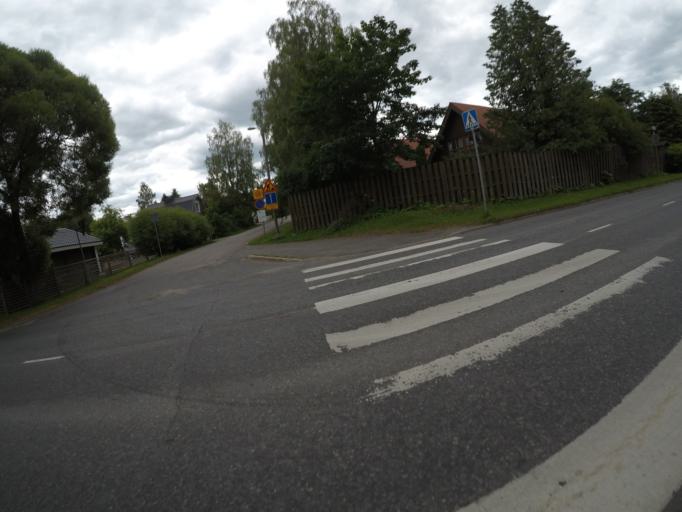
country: FI
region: Haeme
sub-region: Haemeenlinna
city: Haemeenlinna
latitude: 60.9818
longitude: 24.4421
